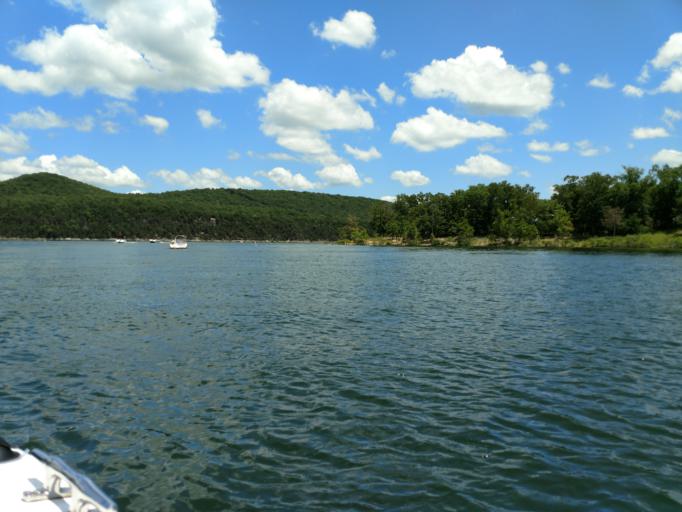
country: US
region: Missouri
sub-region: Barry County
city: Shell Knob
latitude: 36.5948
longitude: -93.5467
